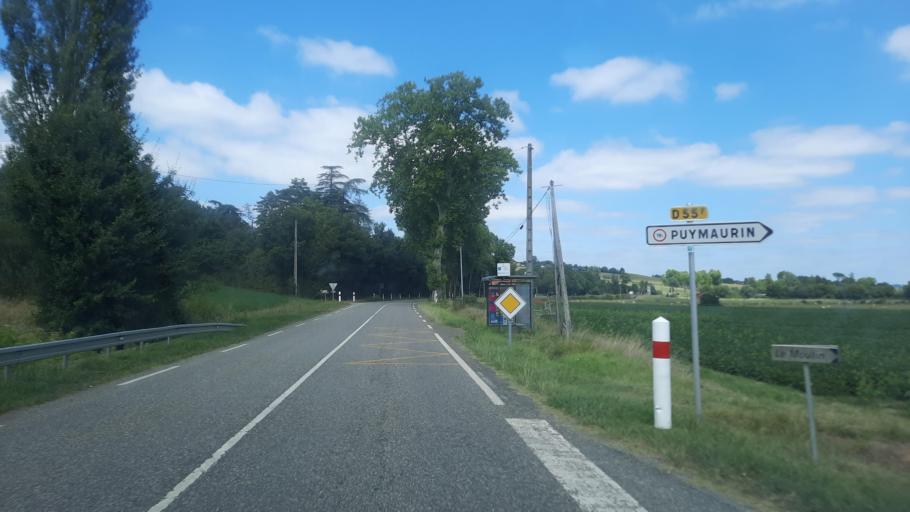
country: FR
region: Midi-Pyrenees
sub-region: Departement de la Haute-Garonne
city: Boulogne-sur-Gesse
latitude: 43.3758
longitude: 0.7553
